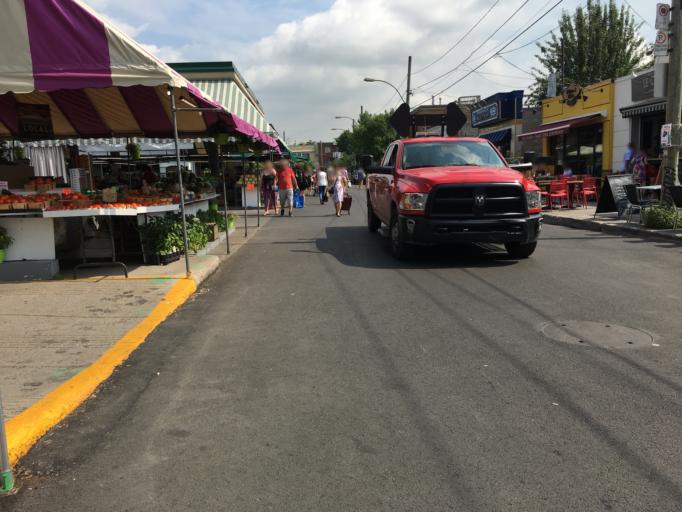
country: CA
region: Quebec
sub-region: Montreal
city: Montreal
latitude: 45.5356
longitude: -73.6146
